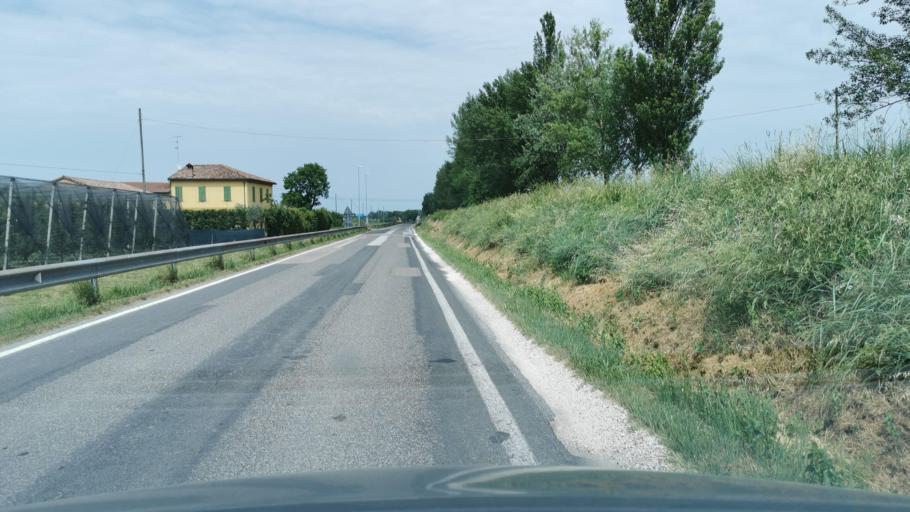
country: IT
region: Emilia-Romagna
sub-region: Provincia di Ravenna
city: Alfonsine
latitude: 44.4778
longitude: 12.0361
